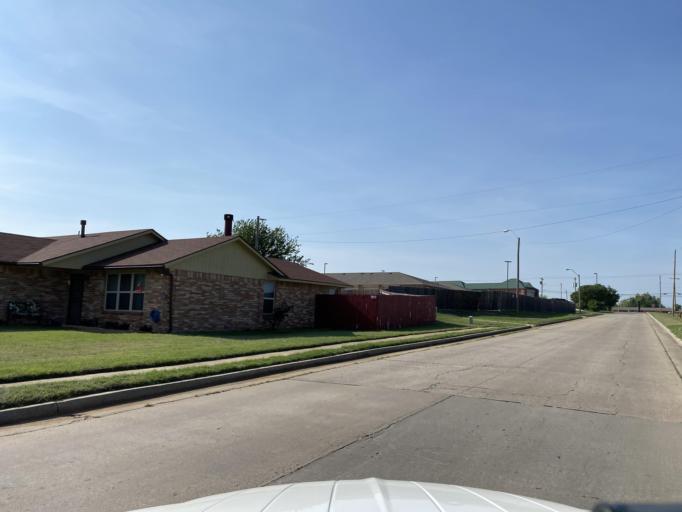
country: US
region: Oklahoma
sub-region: Oklahoma County
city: Spencer
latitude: 35.4914
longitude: -97.3755
